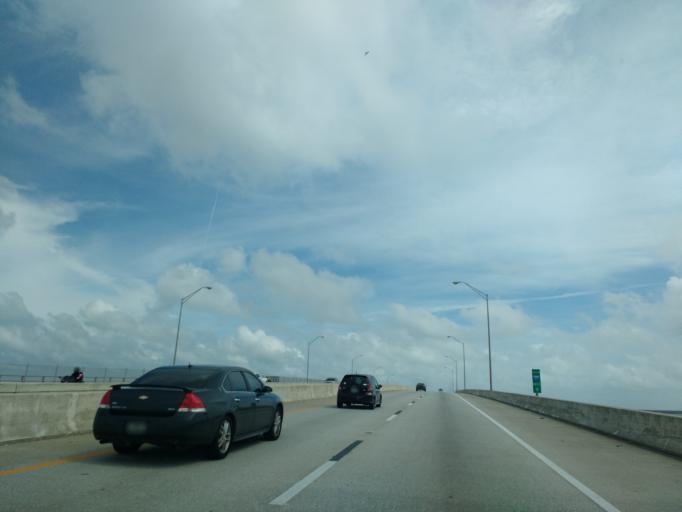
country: US
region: Florida
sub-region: Pinellas County
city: Tierra Verde
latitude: 27.6947
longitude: -82.6793
